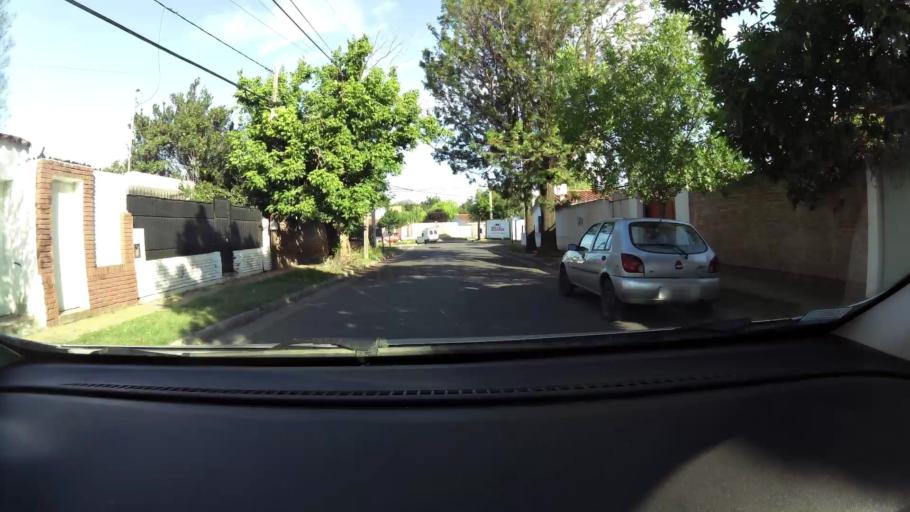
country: AR
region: Cordoba
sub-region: Departamento de Capital
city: Cordoba
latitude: -31.3616
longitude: -64.2269
